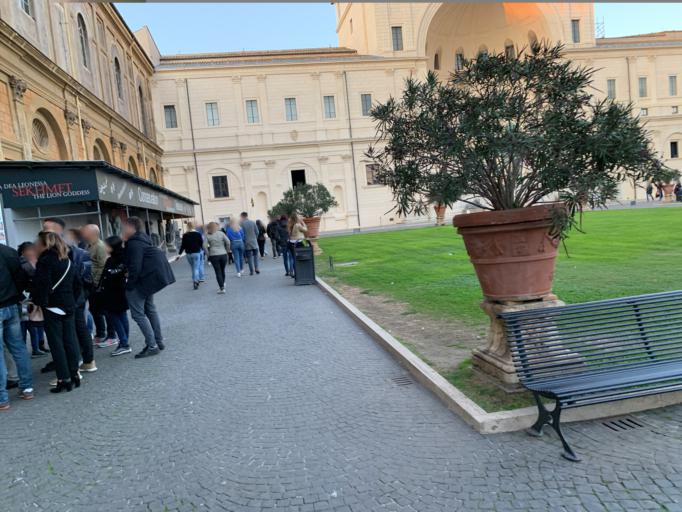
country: VA
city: Vatican City
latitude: 41.9057
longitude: 12.4543
